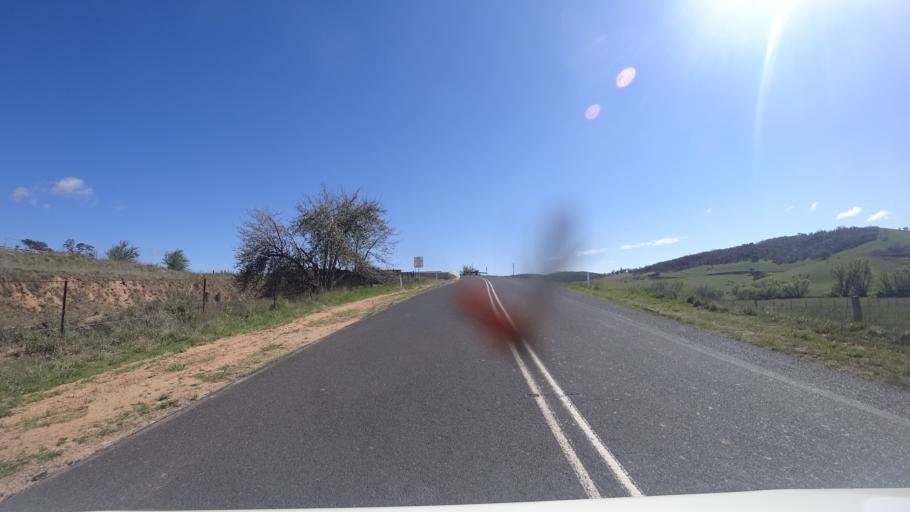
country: AU
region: New South Wales
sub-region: Lithgow
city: Bowenfels
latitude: -33.5170
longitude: 150.0071
